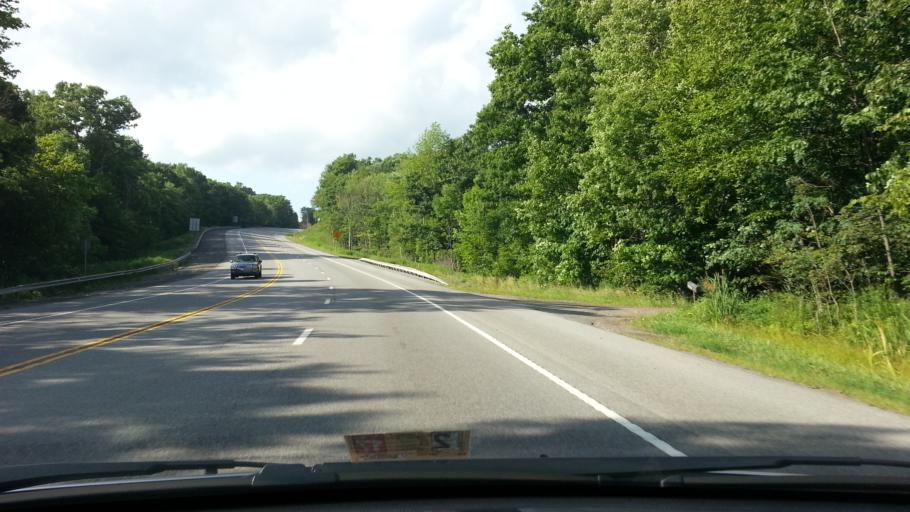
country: US
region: Pennsylvania
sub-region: Elk County
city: Saint Marys
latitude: 41.3143
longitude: -78.5057
